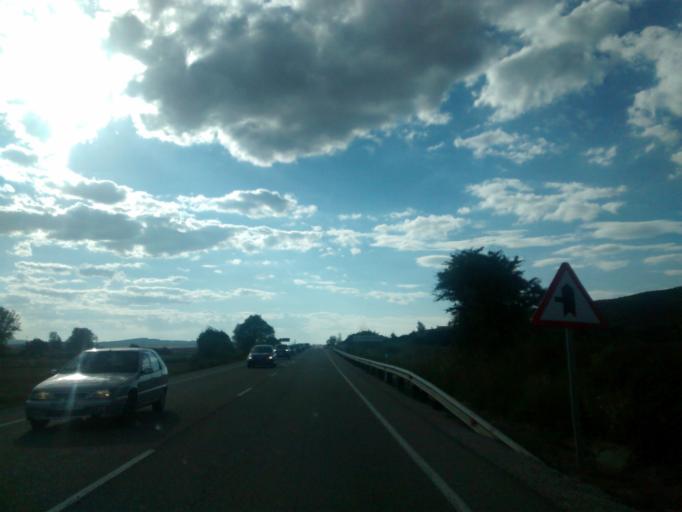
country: ES
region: Castille and Leon
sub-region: Provincia de Burgos
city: Basconcillos del Tozo
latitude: 42.6554
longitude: -3.9003
